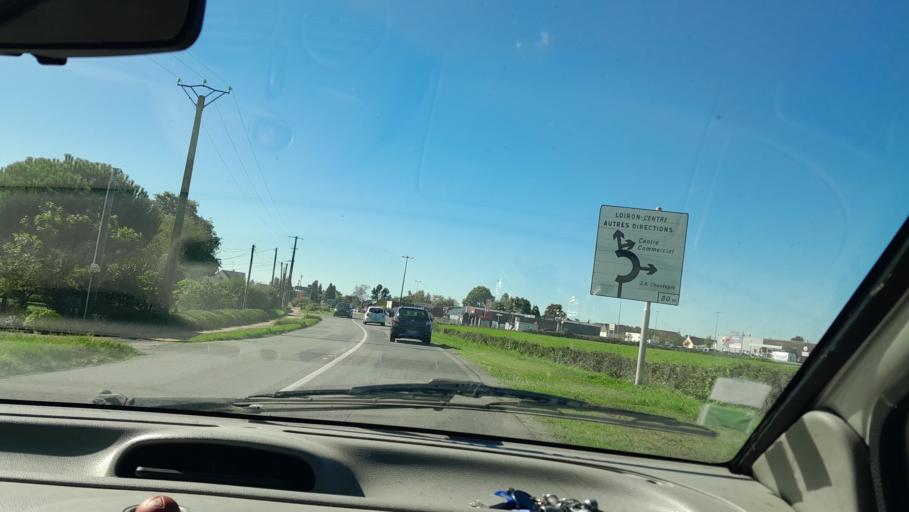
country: FR
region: Pays de la Loire
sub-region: Departement de la Mayenne
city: Loiron
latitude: 48.0668
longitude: -0.9333
